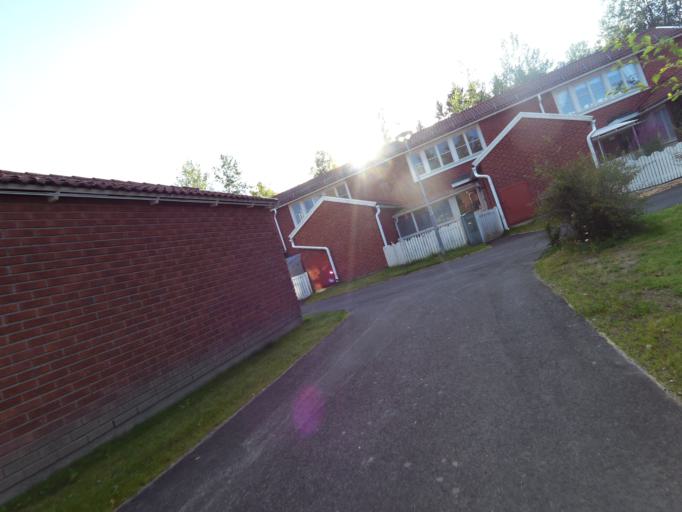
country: SE
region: Gaevleborg
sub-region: Gavle Kommun
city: Gavle
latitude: 60.6488
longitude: 17.1317
